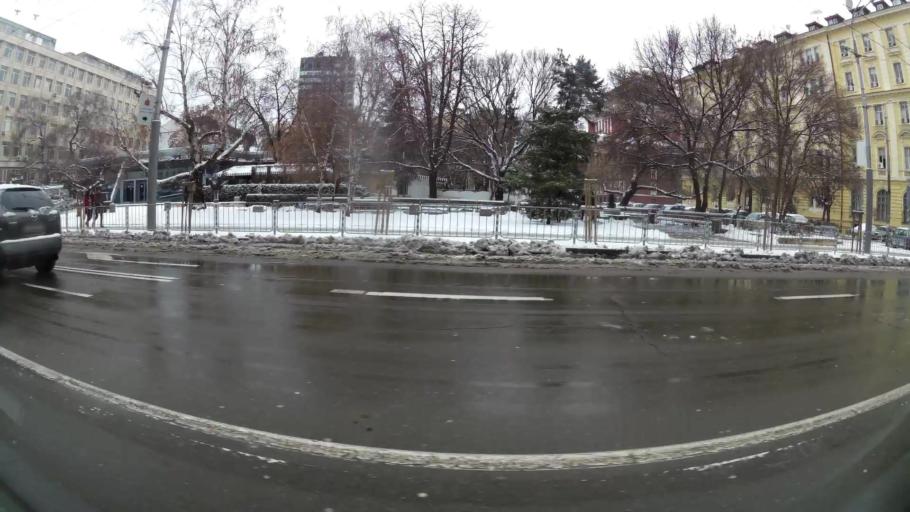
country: BG
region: Sofia-Capital
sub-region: Stolichna Obshtina
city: Sofia
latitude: 42.6931
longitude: 23.3273
